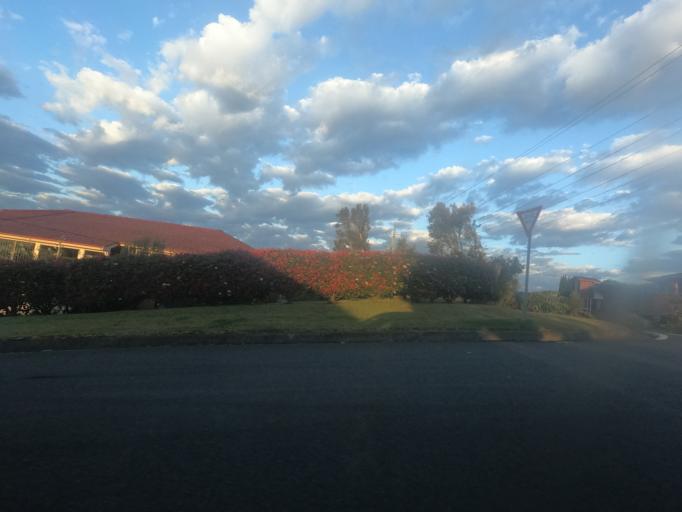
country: AU
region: New South Wales
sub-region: Wollongong
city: Koonawarra
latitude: -34.4959
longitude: 150.8129
